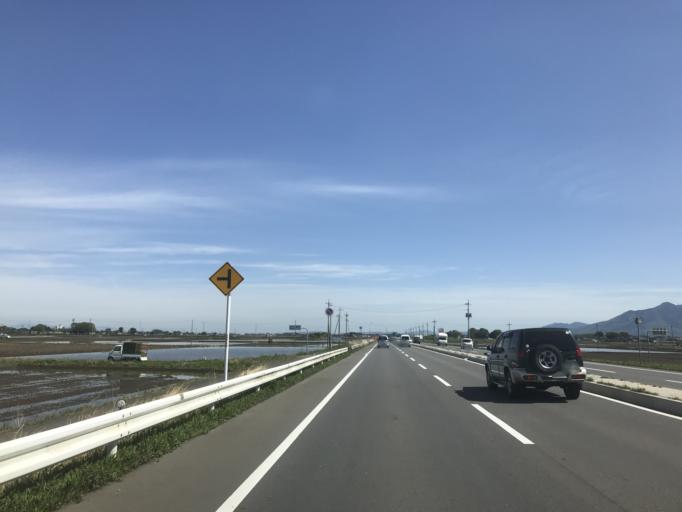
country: JP
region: Ibaraki
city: Ishige
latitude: 36.1366
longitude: 139.9857
